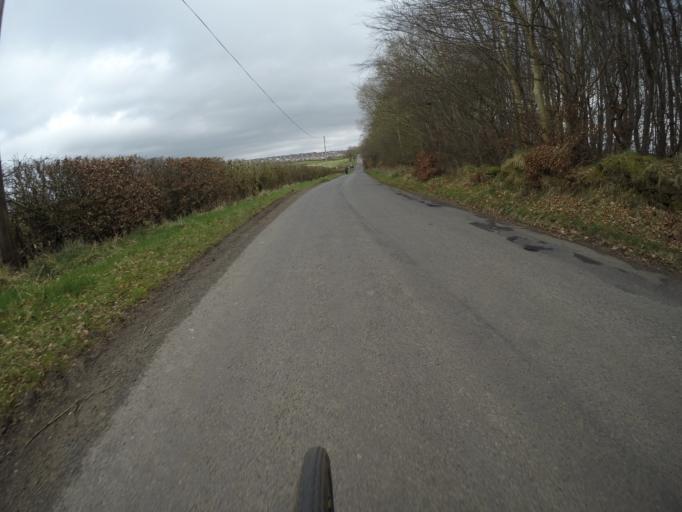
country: GB
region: Scotland
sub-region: East Ayrshire
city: Stewarton
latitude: 55.6782
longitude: -4.5397
